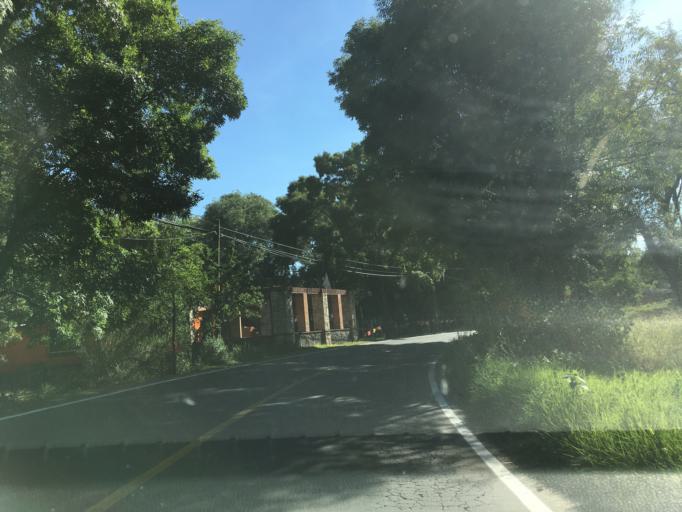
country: MX
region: Hidalgo
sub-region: Omitlan de Juarez
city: San Antonio el Paso
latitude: 20.2173
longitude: -98.5617
